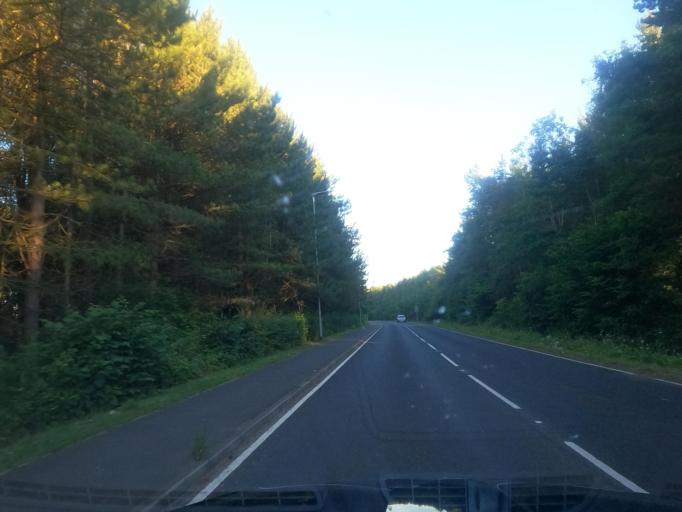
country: GB
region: England
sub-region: Northumberland
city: Seghill
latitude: 55.0796
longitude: -1.5490
